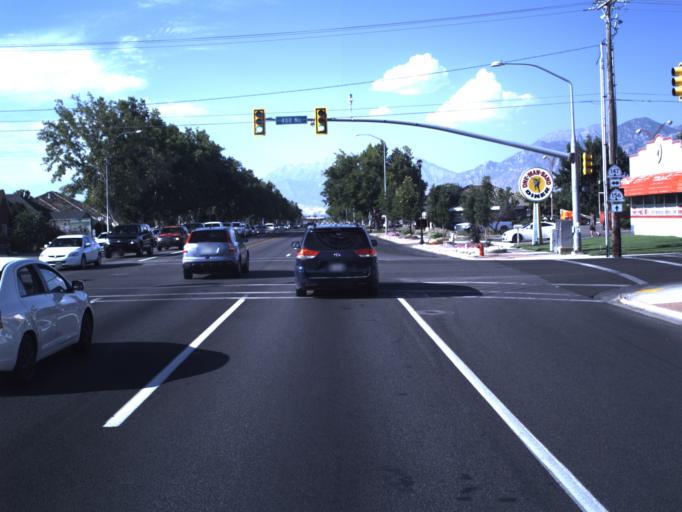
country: US
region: Utah
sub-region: Utah County
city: Spanish Fork
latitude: 40.1147
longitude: -111.6547
